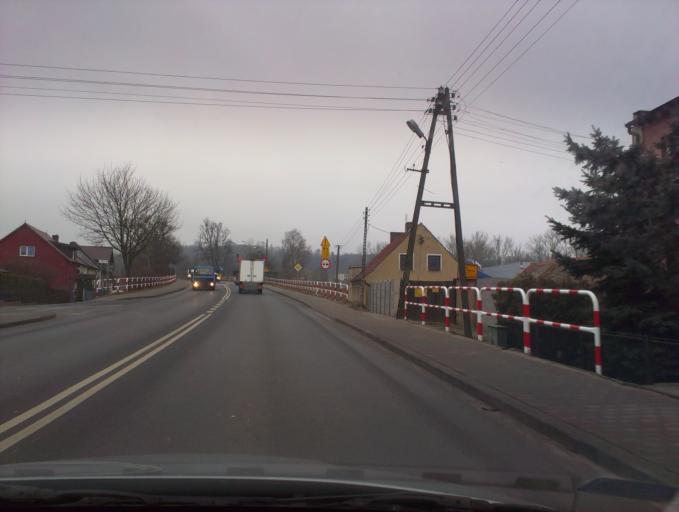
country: PL
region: Greater Poland Voivodeship
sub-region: Powiat pilski
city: Ujscie
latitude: 53.0585
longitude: 16.7283
